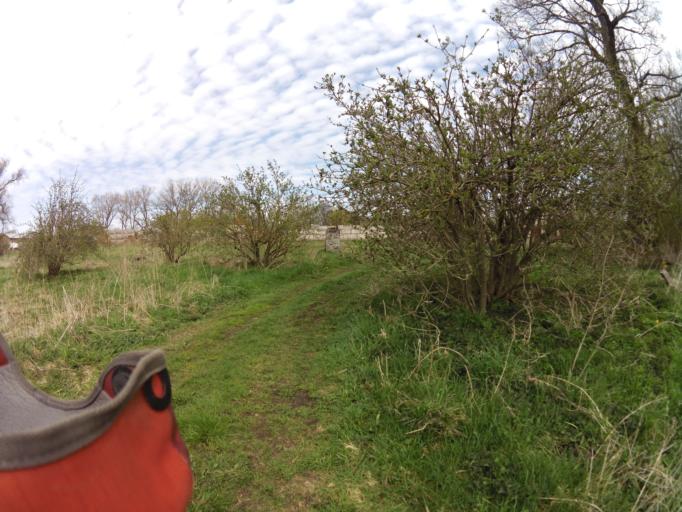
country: PL
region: West Pomeranian Voivodeship
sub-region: Powiat szczecinecki
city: Borne Sulinowo
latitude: 53.7074
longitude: 16.5391
